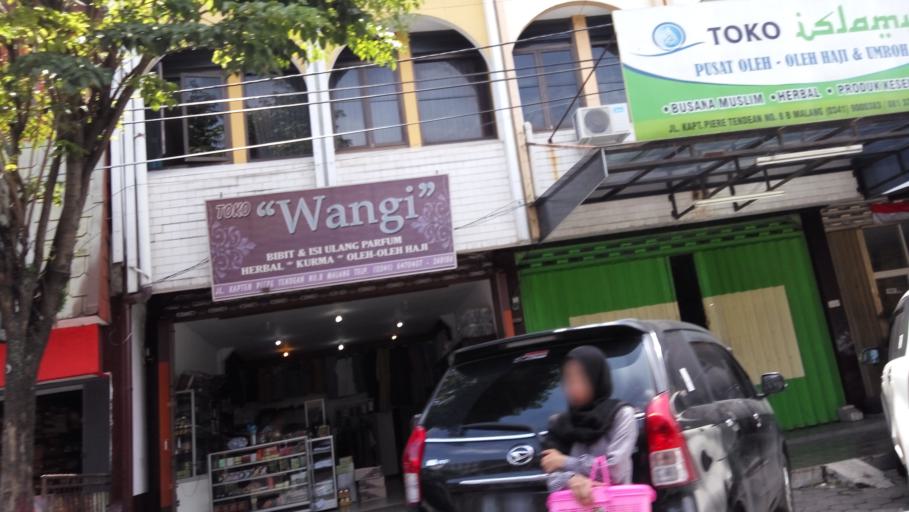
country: ID
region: East Java
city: Malang
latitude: -7.9865
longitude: 112.6291
